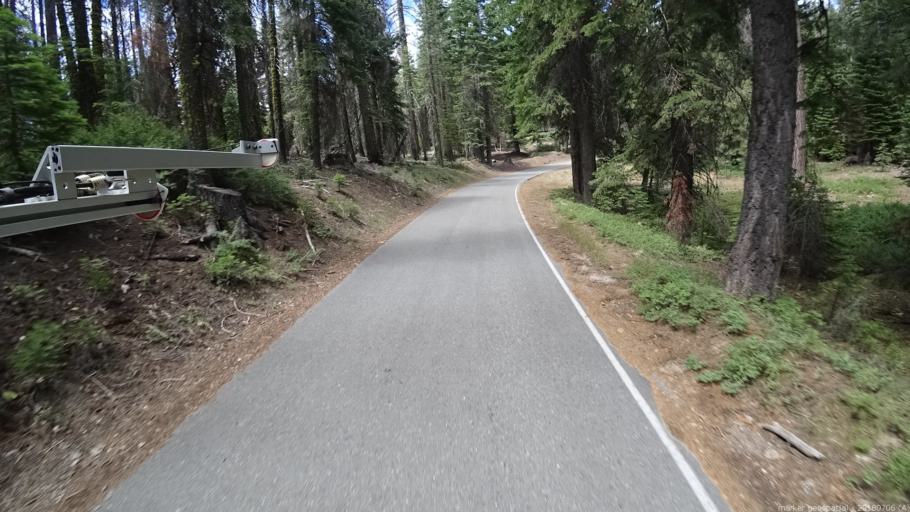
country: US
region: California
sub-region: Madera County
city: Oakhurst
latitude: 37.4293
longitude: -119.4137
